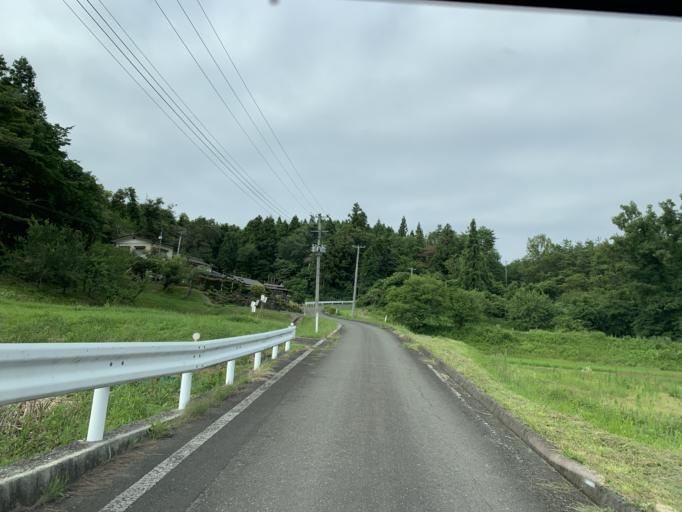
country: JP
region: Iwate
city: Ichinoseki
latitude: 38.8255
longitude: 141.2081
